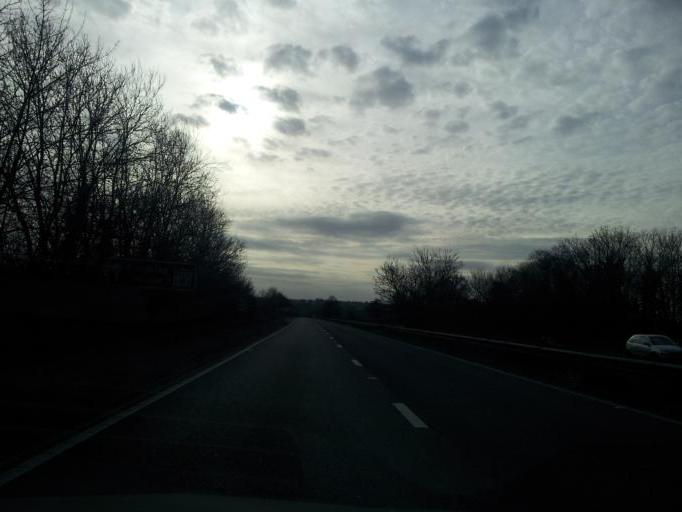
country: GB
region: England
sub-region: District of Rutland
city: Tickencote
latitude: 52.6761
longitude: -0.5354
